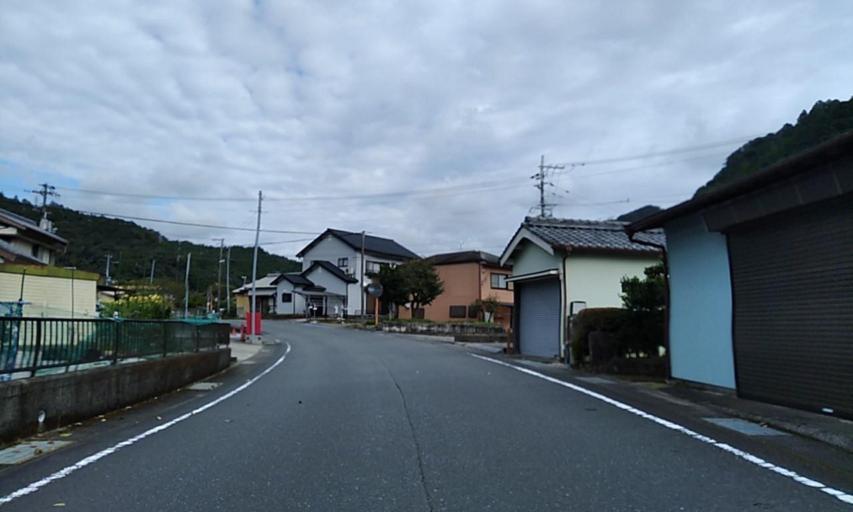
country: JP
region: Wakayama
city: Shingu
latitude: 33.5383
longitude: 135.8208
